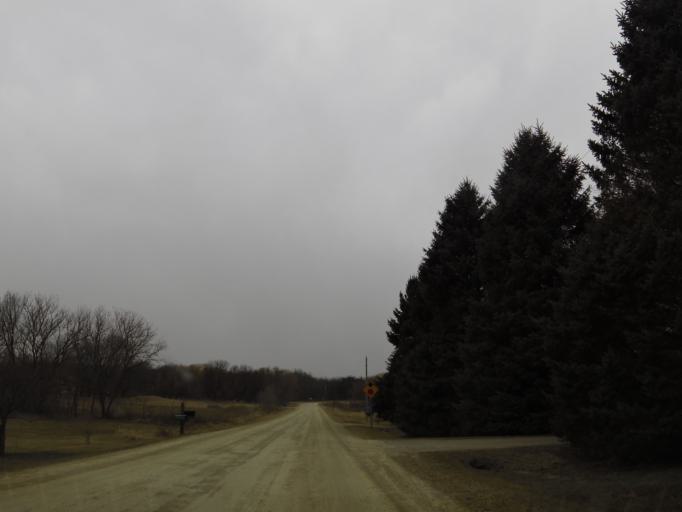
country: US
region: Minnesota
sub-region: Scott County
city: Prior Lake
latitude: 44.6852
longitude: -93.4365
